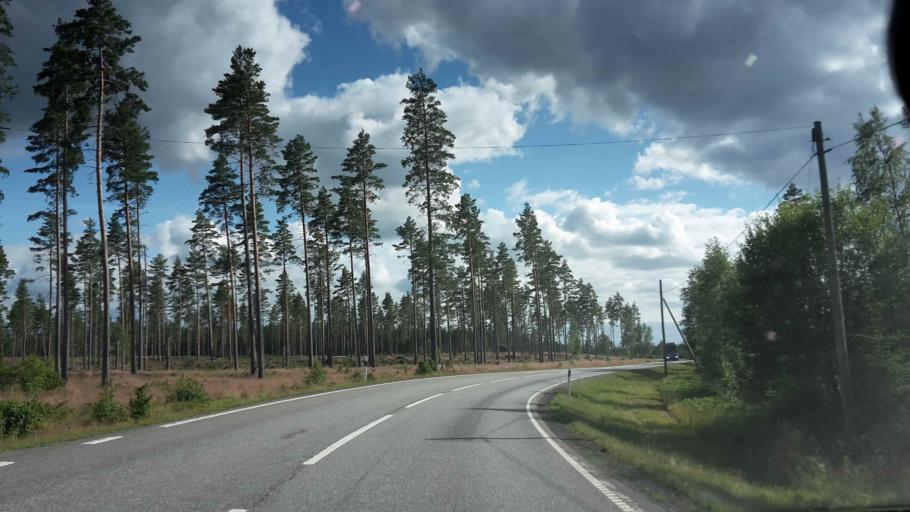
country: SE
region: OErebro
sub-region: Hallsbergs Kommun
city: Palsboda
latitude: 58.8571
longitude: 15.4077
